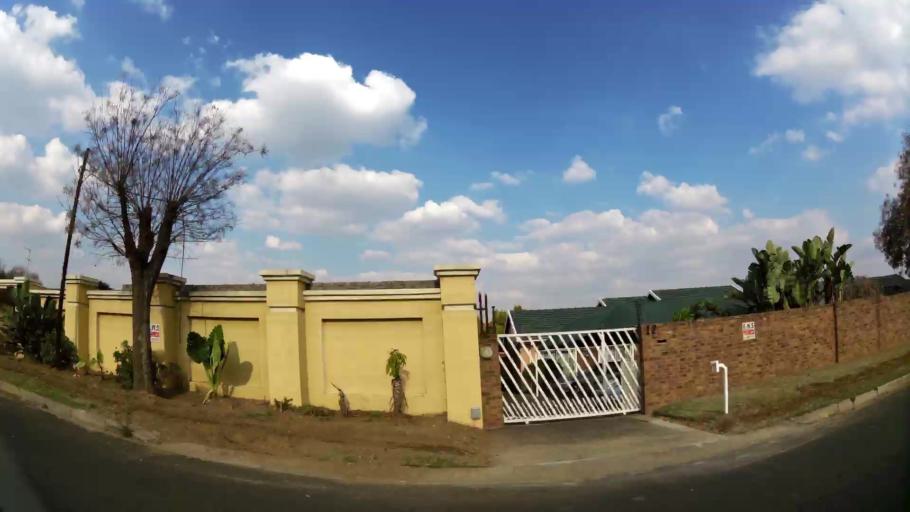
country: ZA
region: Gauteng
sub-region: Ekurhuleni Metropolitan Municipality
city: Germiston
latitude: -26.2466
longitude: 28.1828
